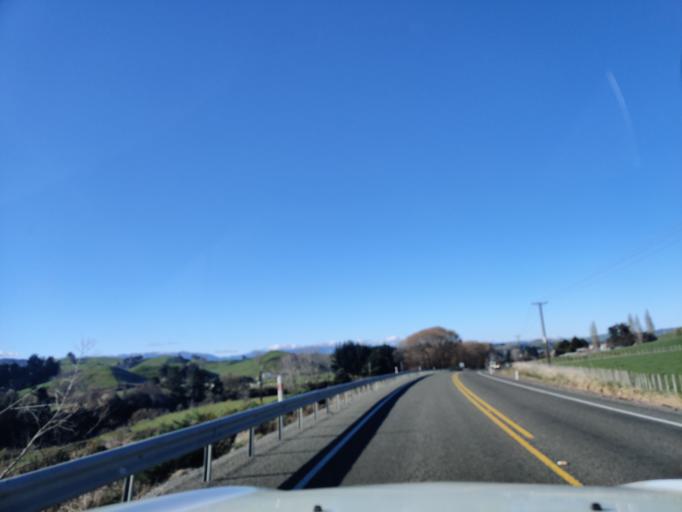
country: NZ
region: Manawatu-Wanganui
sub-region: Ruapehu District
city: Waiouru
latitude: -39.7117
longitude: 175.8375
